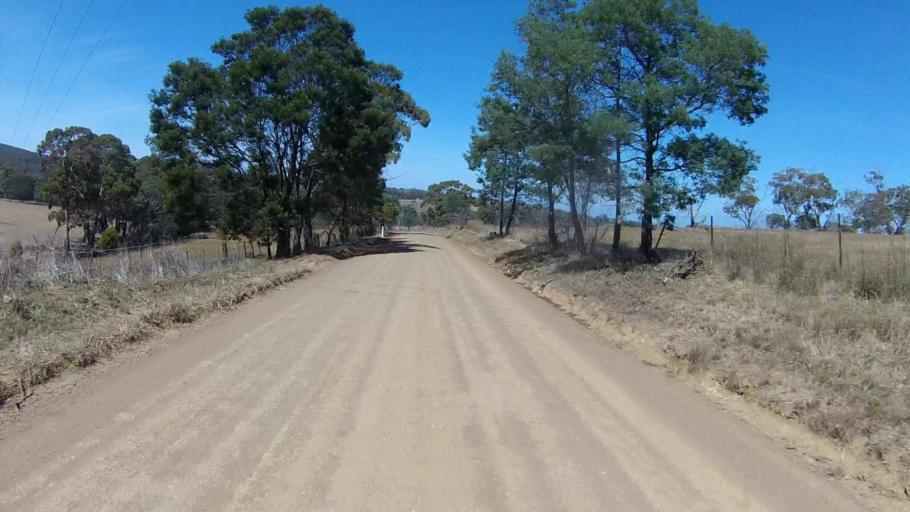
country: AU
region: Tasmania
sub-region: Sorell
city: Sorell
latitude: -42.7966
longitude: 147.6405
